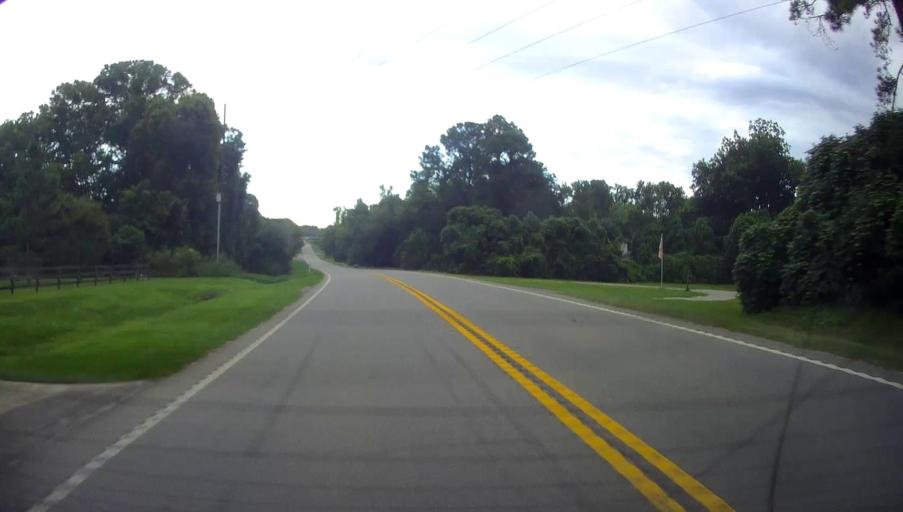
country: US
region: Georgia
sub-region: Houston County
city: Perry
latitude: 32.4161
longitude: -83.6404
